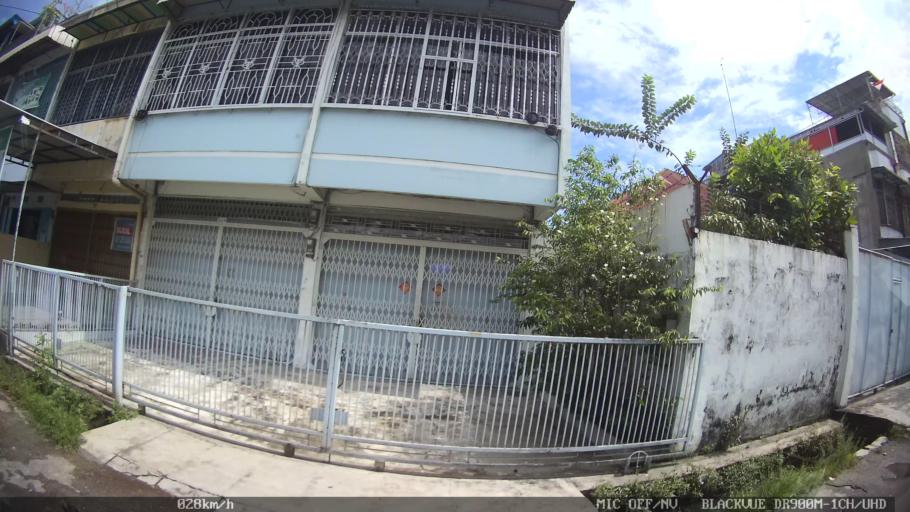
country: ID
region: North Sumatra
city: Medan
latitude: 3.5876
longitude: 98.7086
